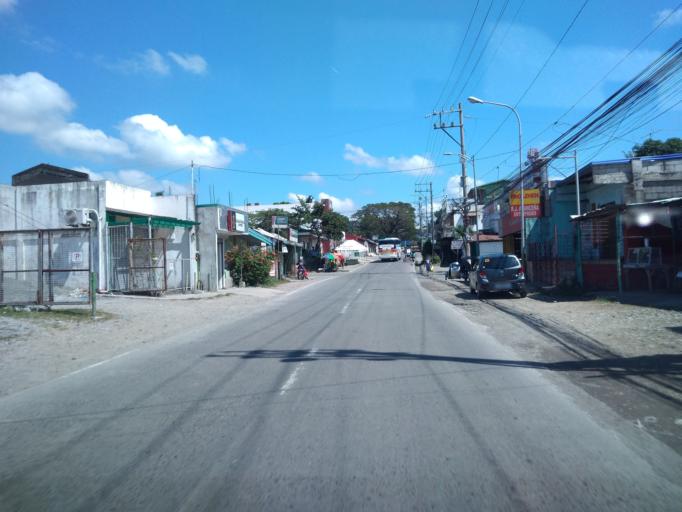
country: PH
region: Central Luzon
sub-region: Province of Bulacan
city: Bitungol
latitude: 14.8592
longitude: 121.0579
